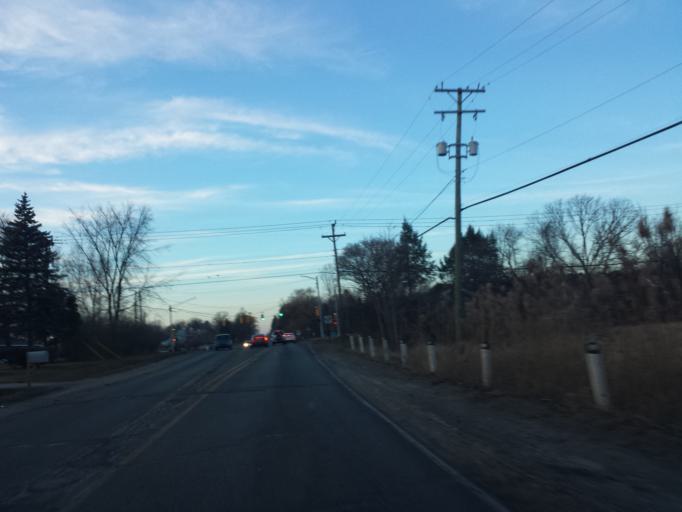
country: US
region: Michigan
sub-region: Oakland County
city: Bloomfield Hills
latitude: 42.6200
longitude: -83.2092
